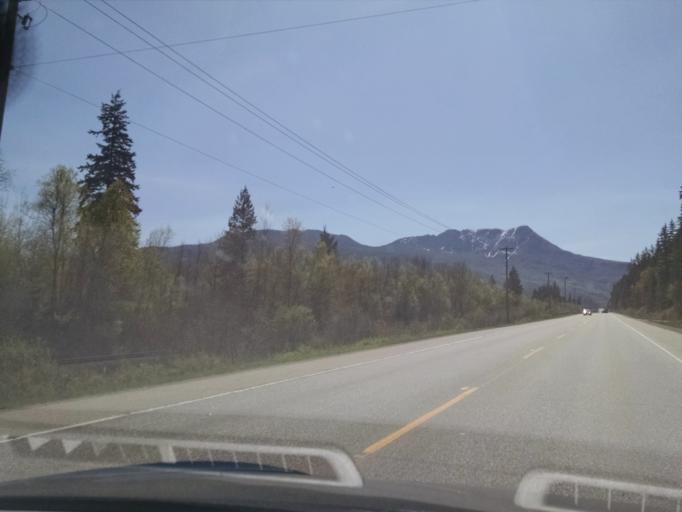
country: CA
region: British Columbia
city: Salmon Arm
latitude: 50.7272
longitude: -119.3162
